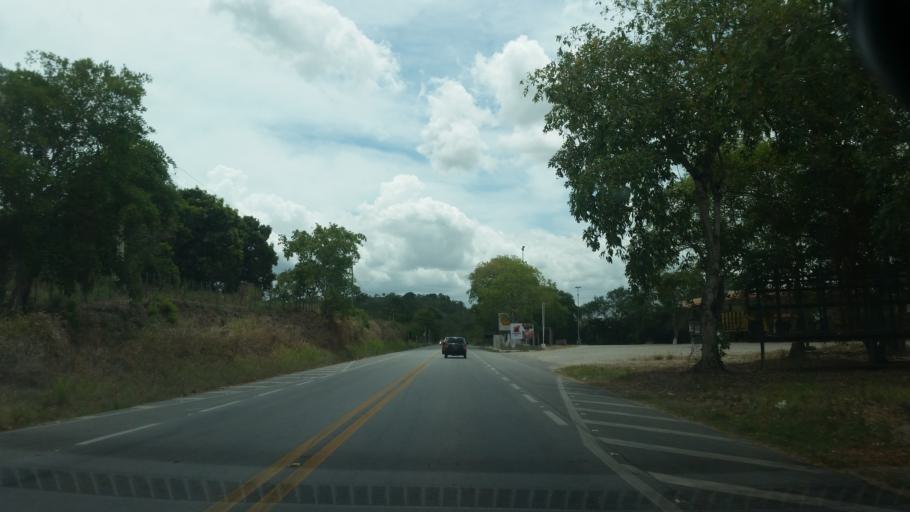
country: BR
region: Alagoas
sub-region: Uniao Dos Palmares
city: Uniao dos Palmares
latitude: -9.1854
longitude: -36.0363
